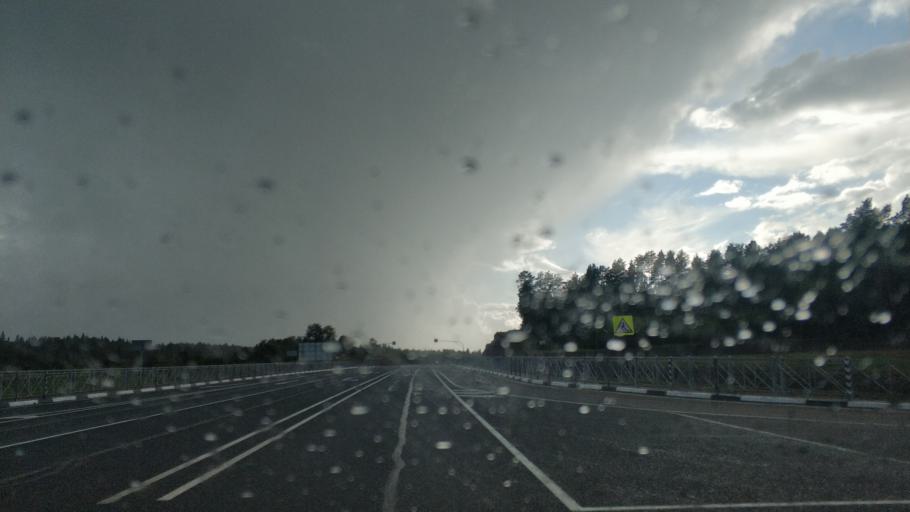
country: RU
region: Leningrad
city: Kuznechnoye
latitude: 61.3393
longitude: 29.8593
